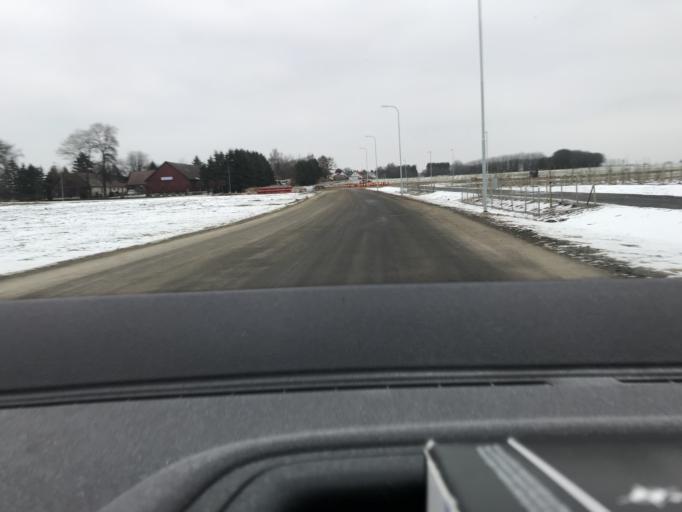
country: SE
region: Skane
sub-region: Ystads Kommun
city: Ystad
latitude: 55.4554
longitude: 13.8527
